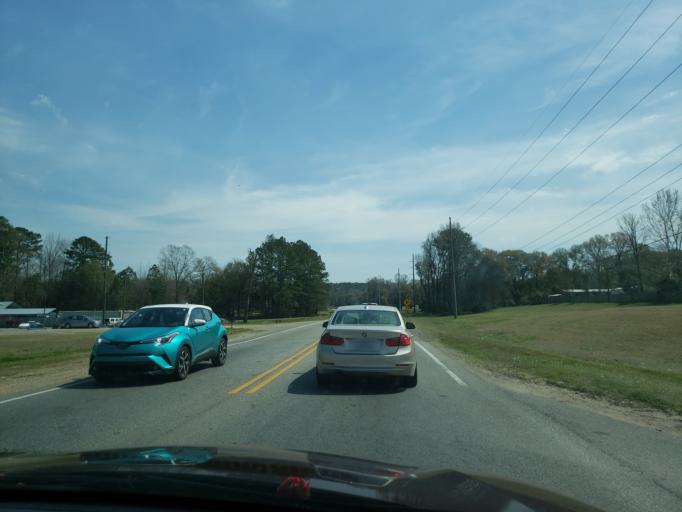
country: US
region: Alabama
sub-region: Autauga County
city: Prattville
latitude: 32.4374
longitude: -86.4709
